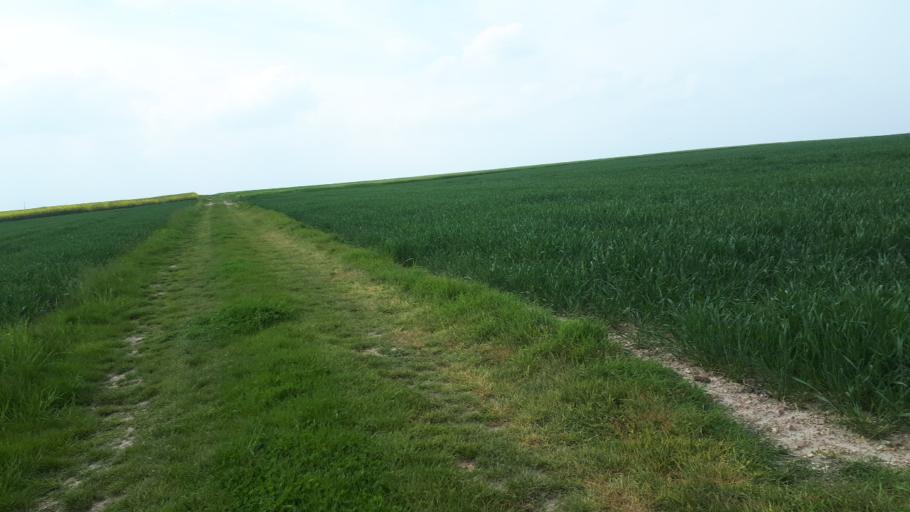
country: FR
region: Centre
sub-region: Departement du Loir-et-Cher
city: Lunay
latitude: 47.8252
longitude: 0.9334
